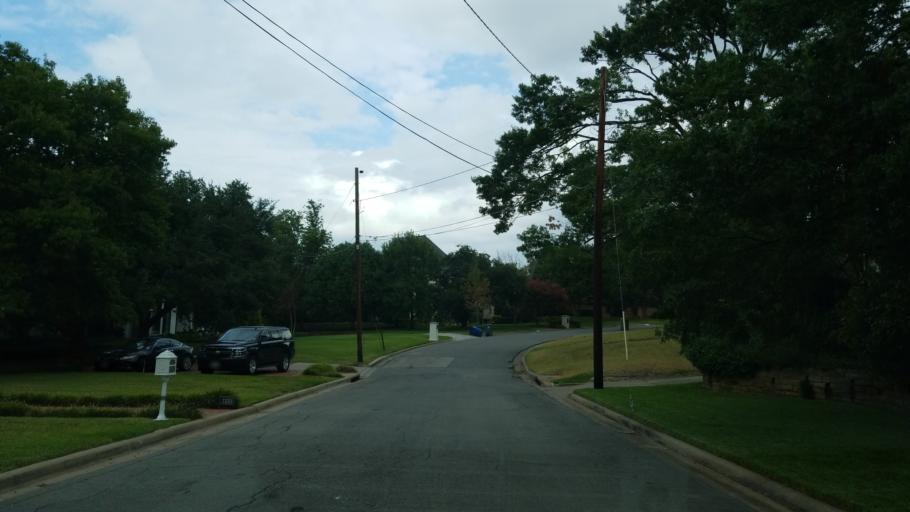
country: US
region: Texas
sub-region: Dallas County
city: Richardson
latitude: 32.9388
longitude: -96.7813
